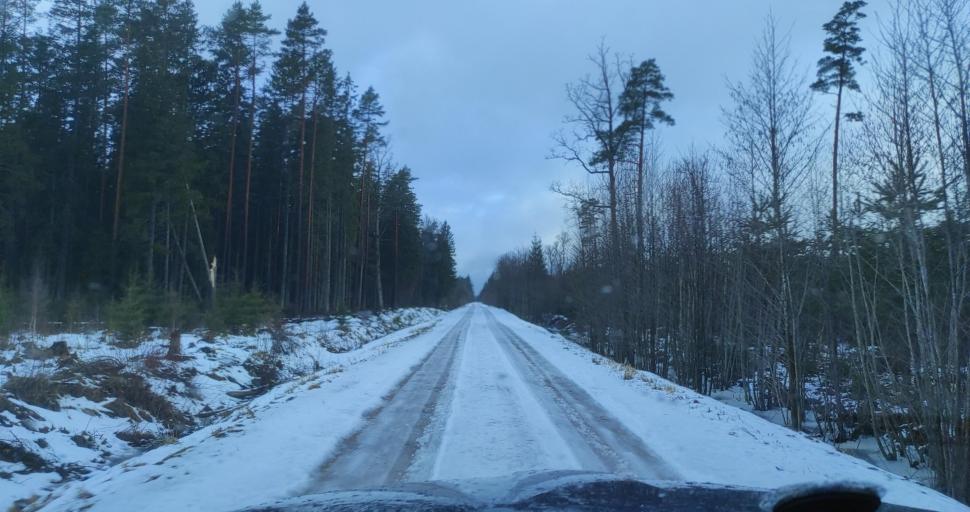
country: LV
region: Dundaga
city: Dundaga
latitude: 57.4073
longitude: 22.0905
